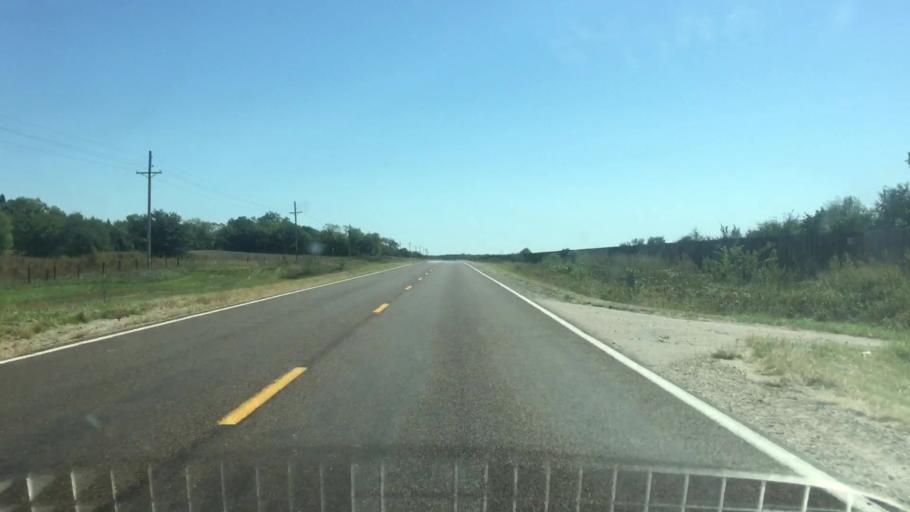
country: US
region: Nebraska
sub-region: Jefferson County
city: Fairbury
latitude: 40.0943
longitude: -97.1288
